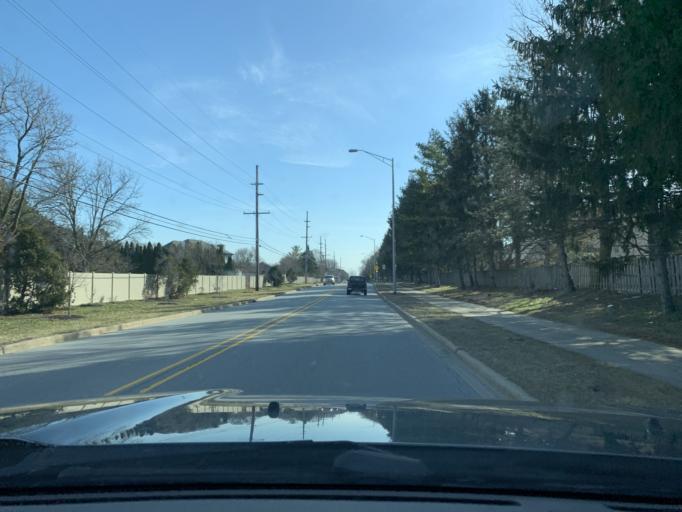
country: US
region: Indiana
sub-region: Lake County
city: Munster
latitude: 41.5290
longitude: -87.4904
